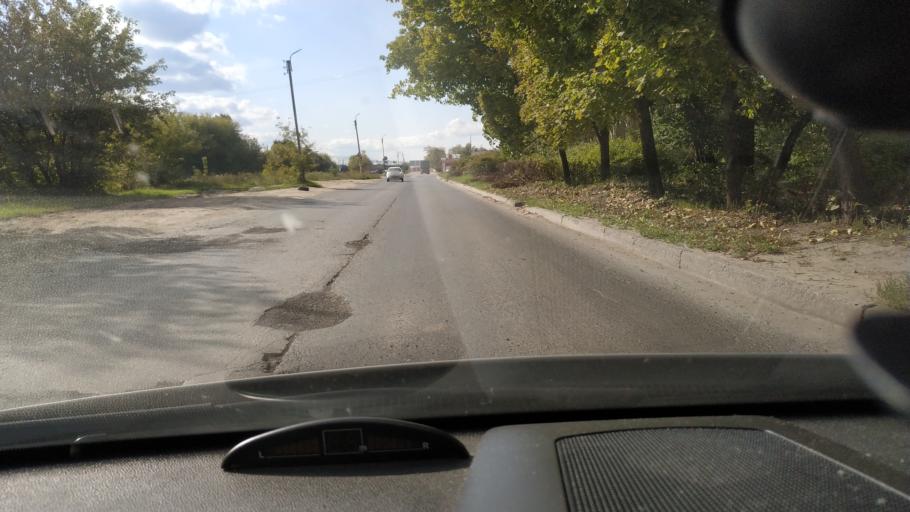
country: RU
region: Rjazan
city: Ryazan'
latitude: 54.6513
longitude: 39.6479
